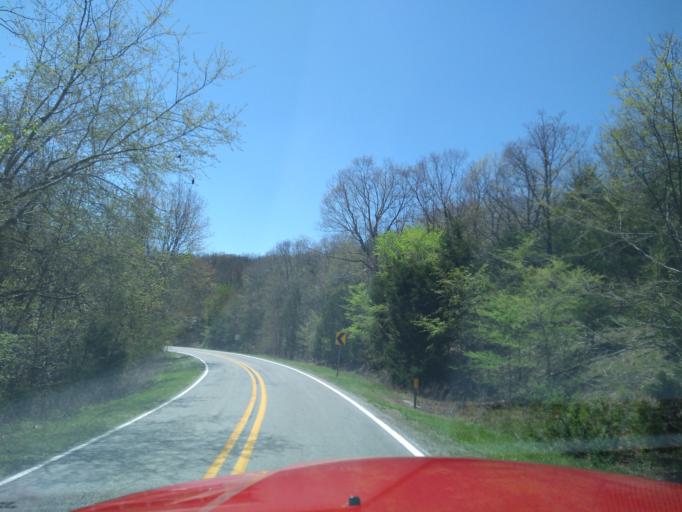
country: US
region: Arkansas
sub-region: Washington County
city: West Fork
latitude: 35.7912
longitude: -94.2554
